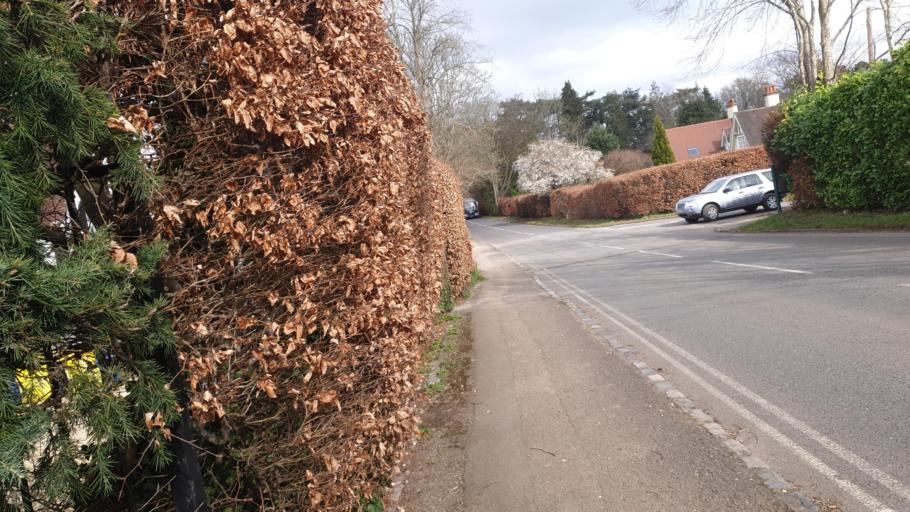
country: GB
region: England
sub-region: Oxfordshire
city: Boars Hill
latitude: 51.7158
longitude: -1.2820
